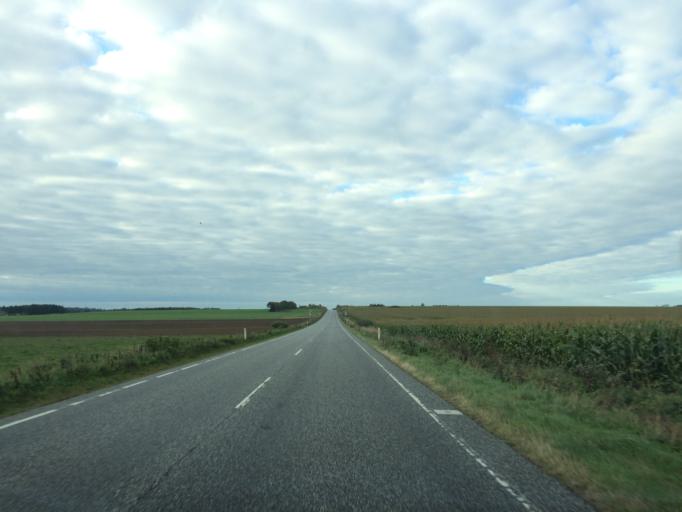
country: DK
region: Central Jutland
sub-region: Ringkobing-Skjern Kommune
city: Skjern
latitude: 56.0087
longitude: 8.5030
